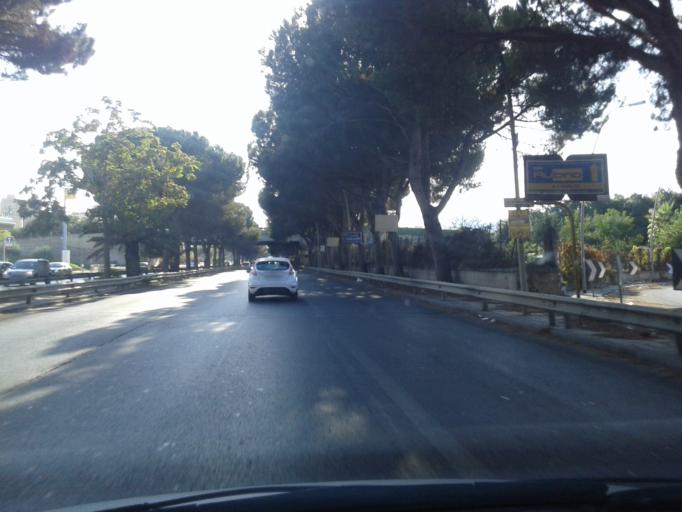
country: IT
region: Sicily
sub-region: Palermo
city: Ciaculli
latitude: 38.0886
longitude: 13.3675
